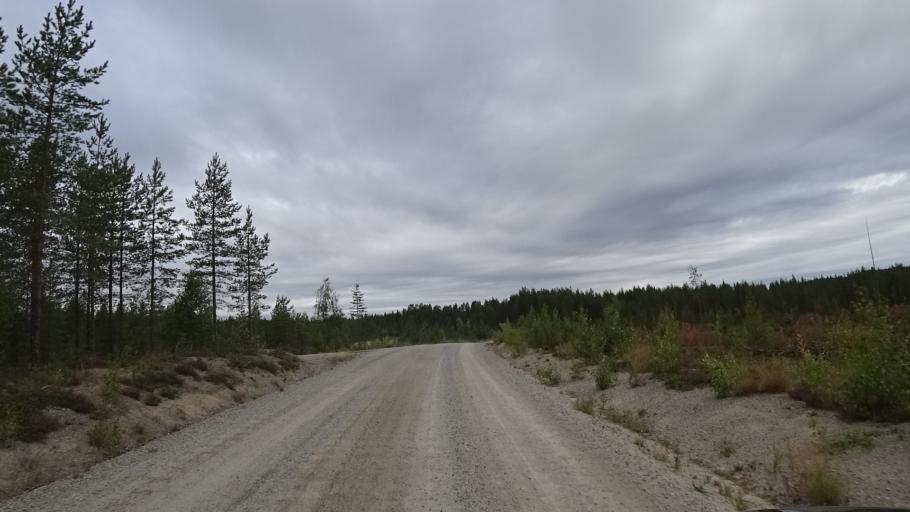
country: FI
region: North Karelia
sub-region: Pielisen Karjala
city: Lieksa
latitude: 63.2524
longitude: 30.3275
